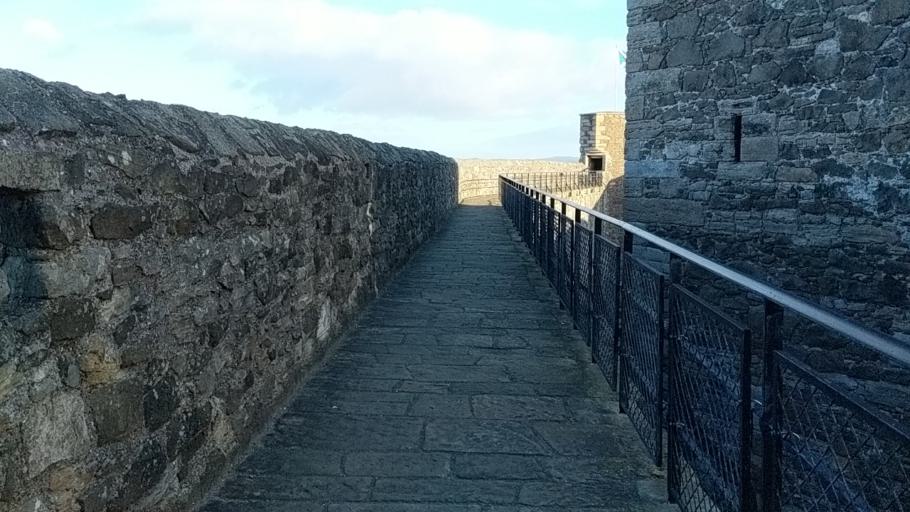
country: GB
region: Scotland
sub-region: Fife
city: Crossford
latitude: 56.0062
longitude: -3.5162
